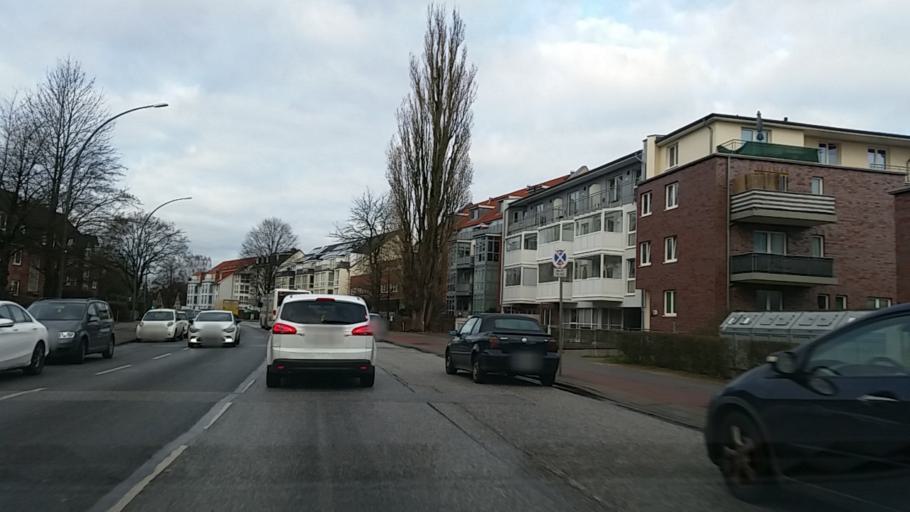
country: DE
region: Hamburg
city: Eidelstedt
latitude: 53.5959
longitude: 9.8676
